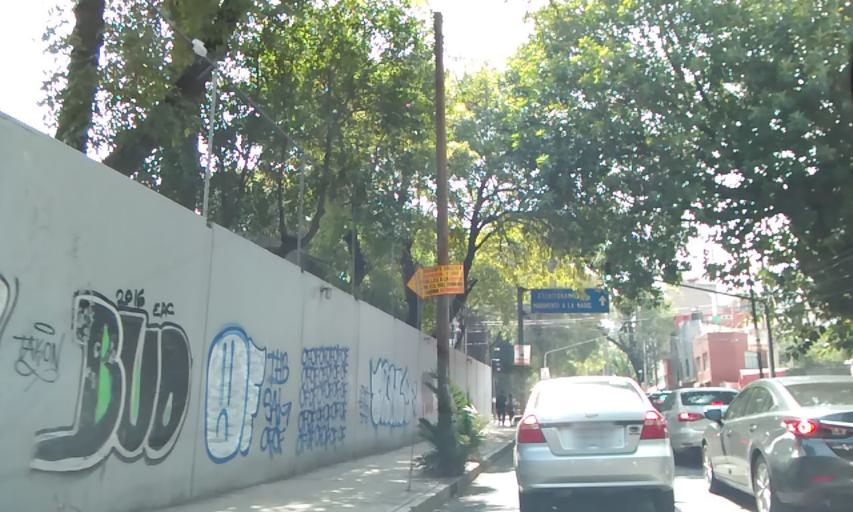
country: MX
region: Mexico City
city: Cuauhtemoc
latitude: 19.4330
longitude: -99.1635
